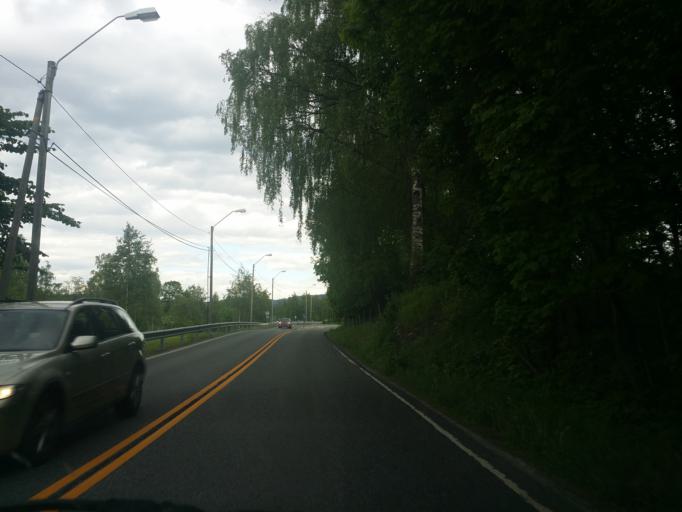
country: NO
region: Akershus
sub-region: Baerum
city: Lysaker
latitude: 59.9396
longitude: 10.5777
